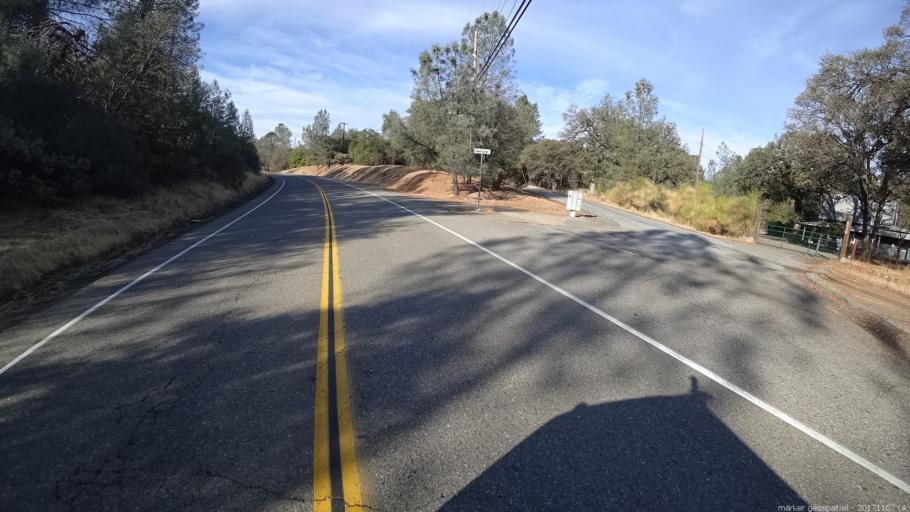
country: US
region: California
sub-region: Shasta County
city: Shasta
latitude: 40.5530
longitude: -122.4500
